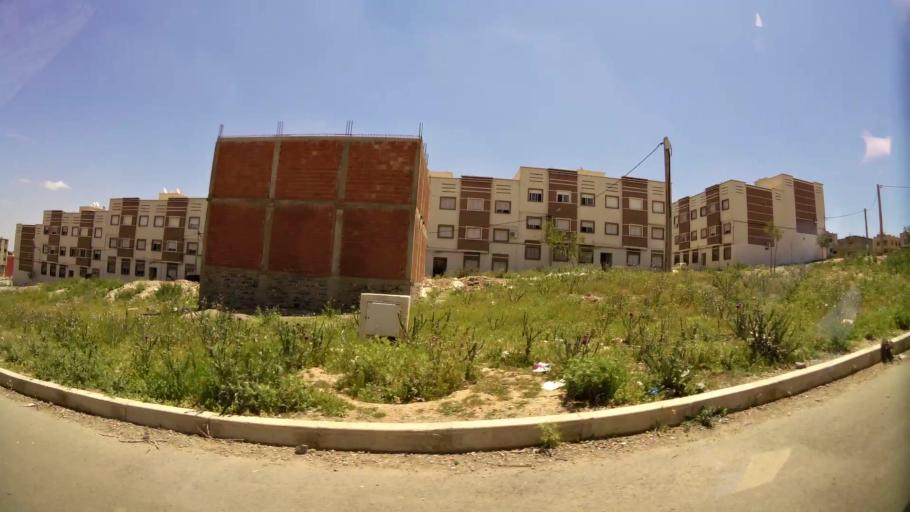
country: MA
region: Oriental
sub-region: Oujda-Angad
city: Oujda
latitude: 34.6553
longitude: -1.9432
